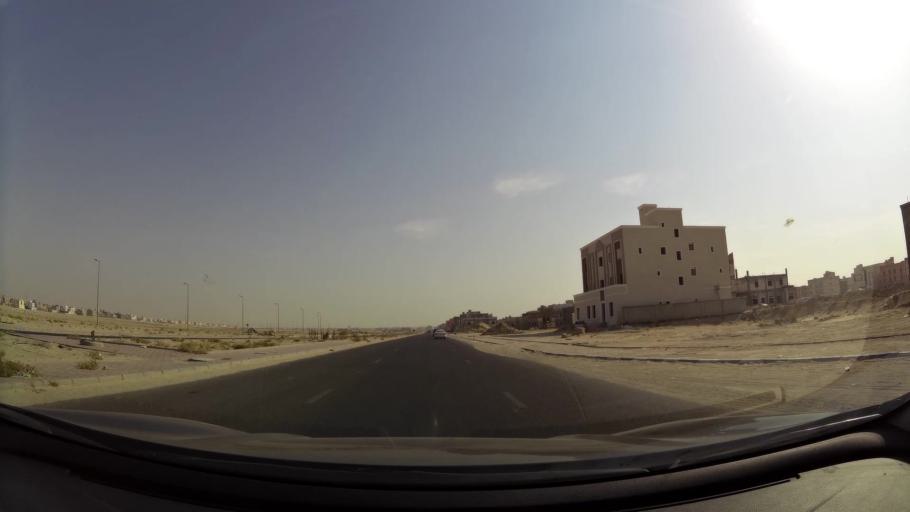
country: KW
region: Al Ahmadi
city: Al Wafrah
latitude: 28.7772
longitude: 48.0598
